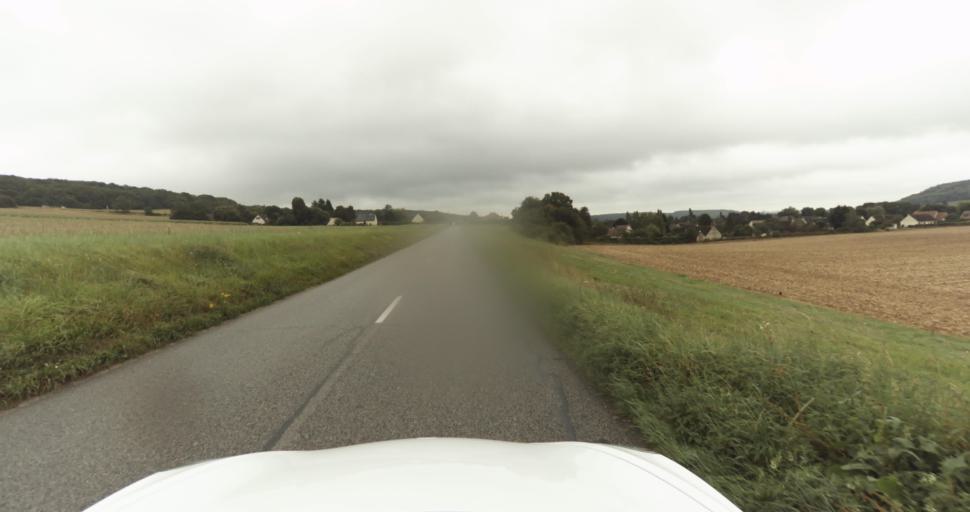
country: FR
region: Haute-Normandie
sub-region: Departement de l'Eure
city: Normanville
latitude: 49.0733
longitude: 1.1683
